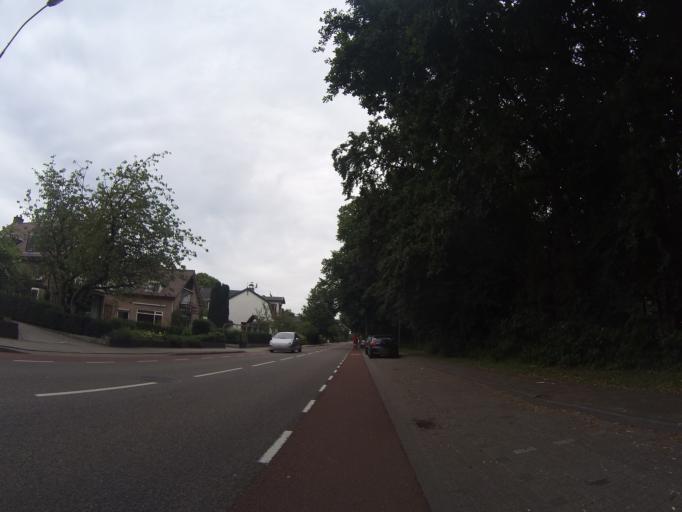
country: NL
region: Utrecht
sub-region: Gemeente Baarn
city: Baarn
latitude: 52.2156
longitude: 5.2783
